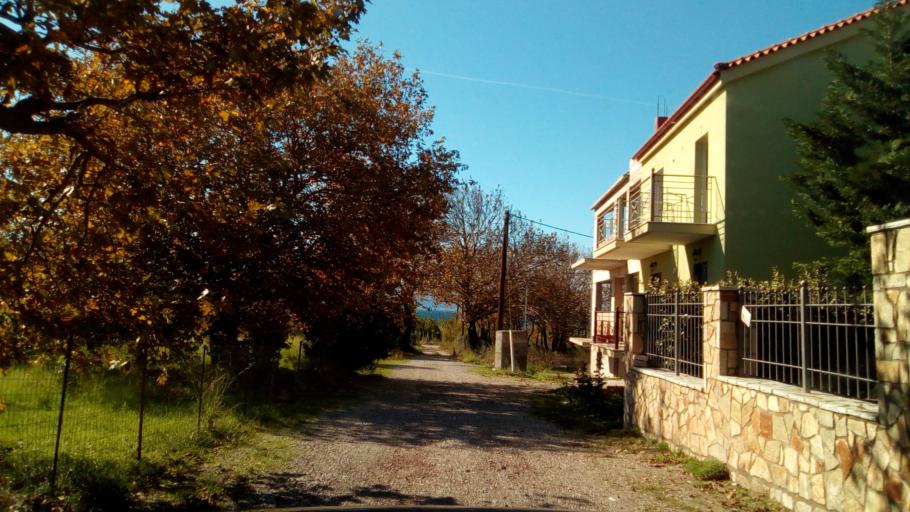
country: GR
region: West Greece
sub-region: Nomos Achaias
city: Kamarai
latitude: 38.3934
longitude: 22.0003
